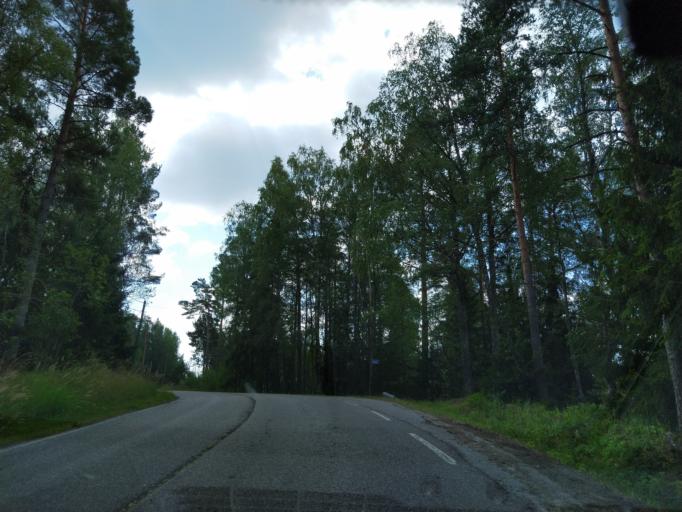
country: FI
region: Uusimaa
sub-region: Helsinki
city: Kirkkonummi
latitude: 60.0925
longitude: 24.5020
